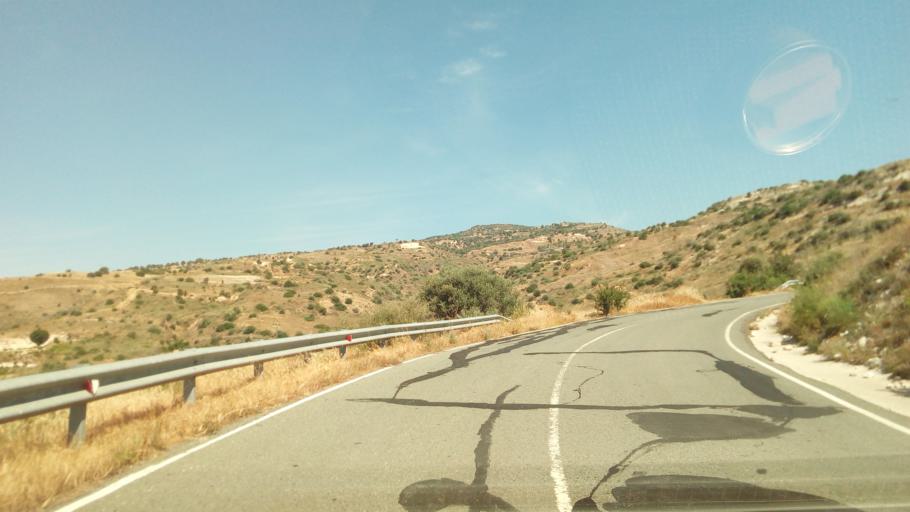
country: CY
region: Limassol
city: Pachna
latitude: 34.7912
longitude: 32.6919
